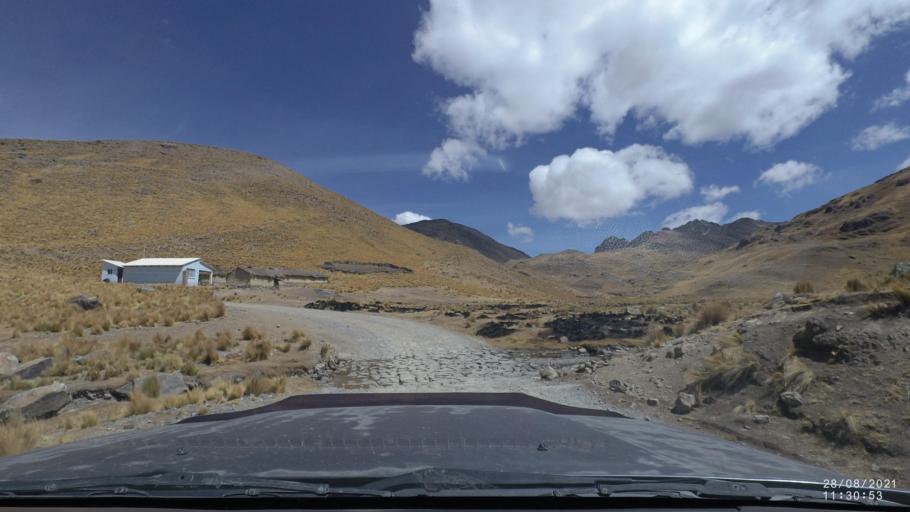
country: BO
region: Cochabamba
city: Sipe Sipe
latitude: -17.1797
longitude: -66.3657
